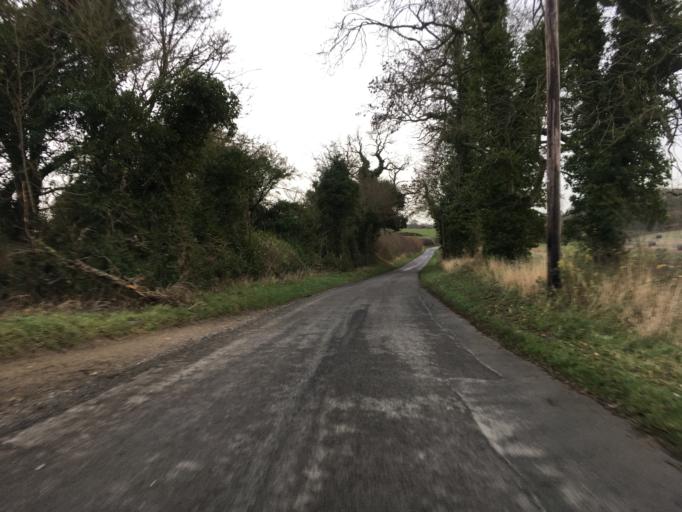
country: GB
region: England
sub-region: Wiltshire
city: Nettleton
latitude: 51.5125
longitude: -2.2817
